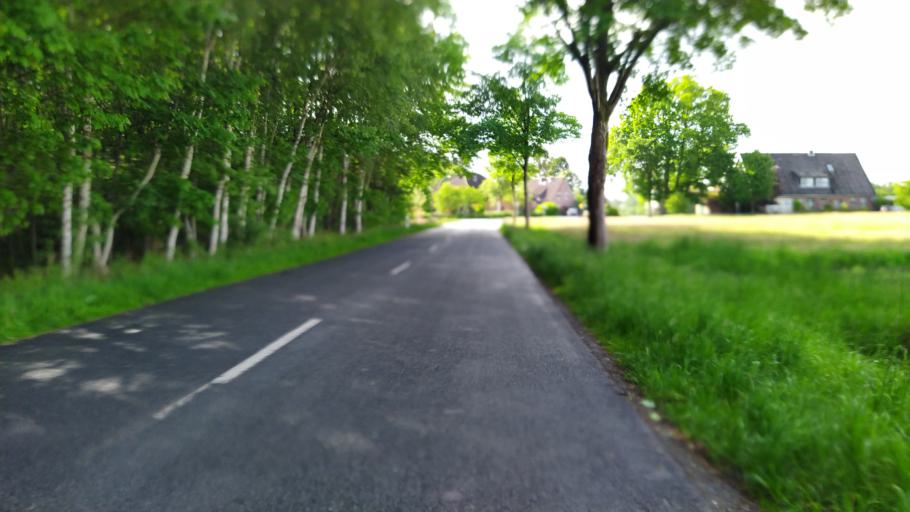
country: DE
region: Lower Saxony
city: Brest
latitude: 53.4338
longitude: 9.3547
